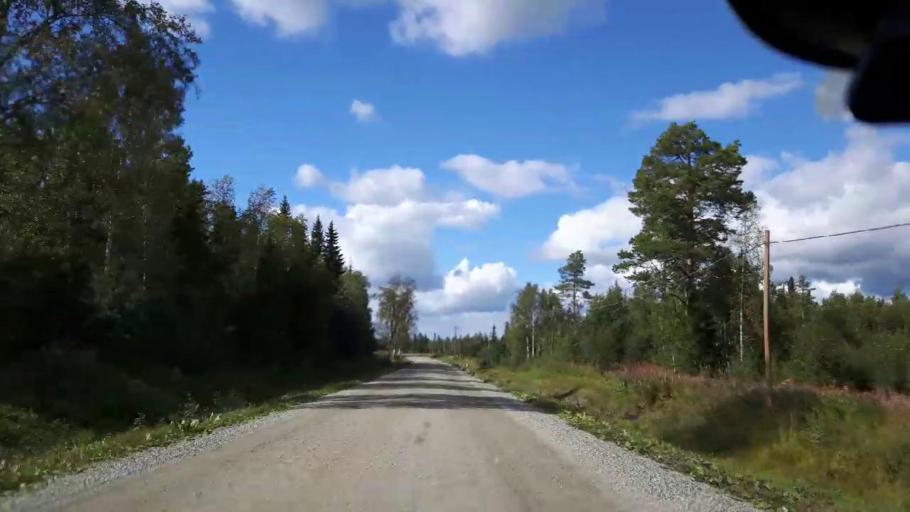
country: SE
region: Jaemtland
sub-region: Stroemsunds Kommun
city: Stroemsund
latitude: 63.3068
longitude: 15.6022
